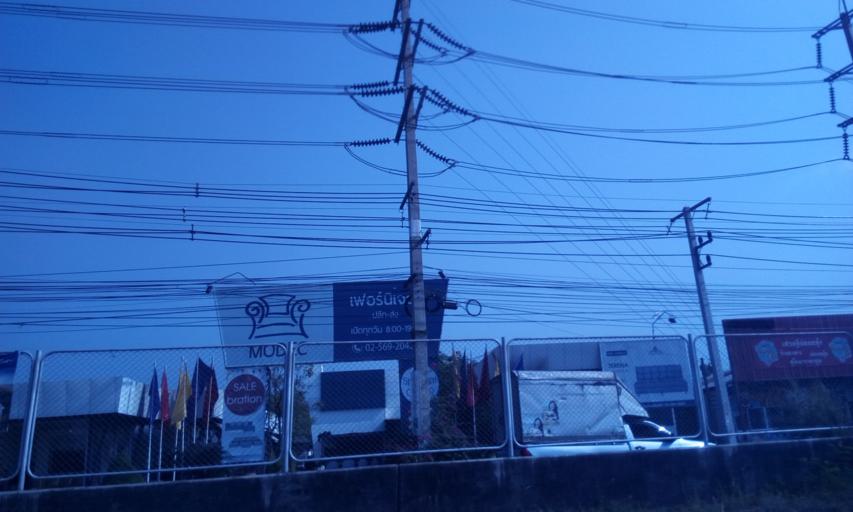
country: TH
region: Pathum Thani
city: Lam Luk Ka
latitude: 13.9338
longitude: 100.7070
